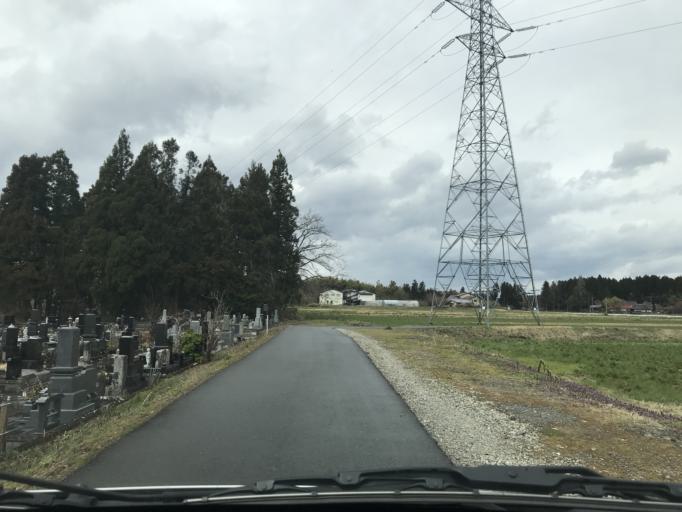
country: JP
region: Iwate
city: Mizusawa
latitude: 39.0969
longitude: 141.1034
